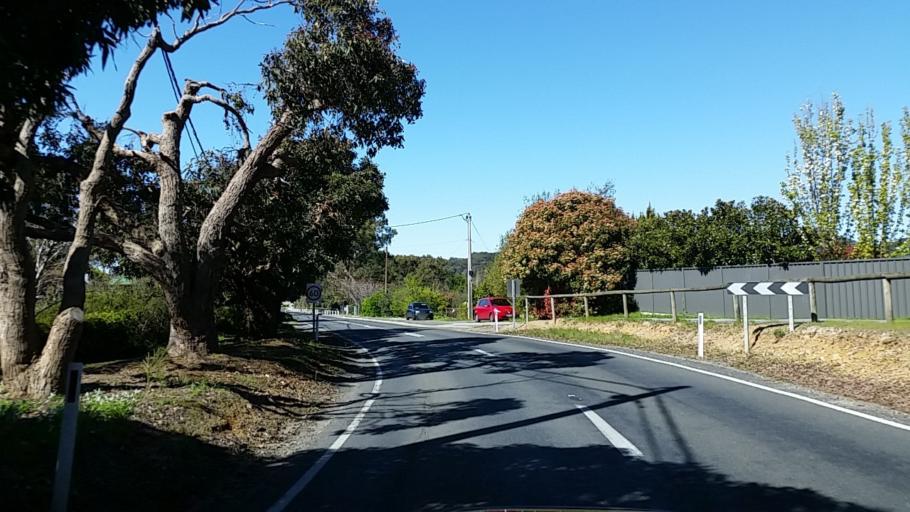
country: AU
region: South Australia
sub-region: Adelaide Hills
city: Bridgewater
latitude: -34.9595
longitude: 138.7345
